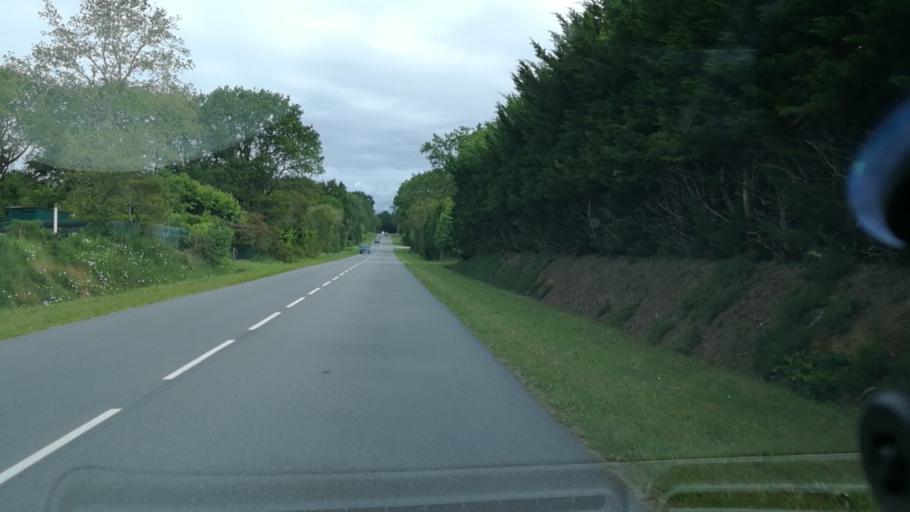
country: FR
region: Brittany
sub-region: Departement du Morbihan
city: Penestin
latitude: 47.4634
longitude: -2.4780
